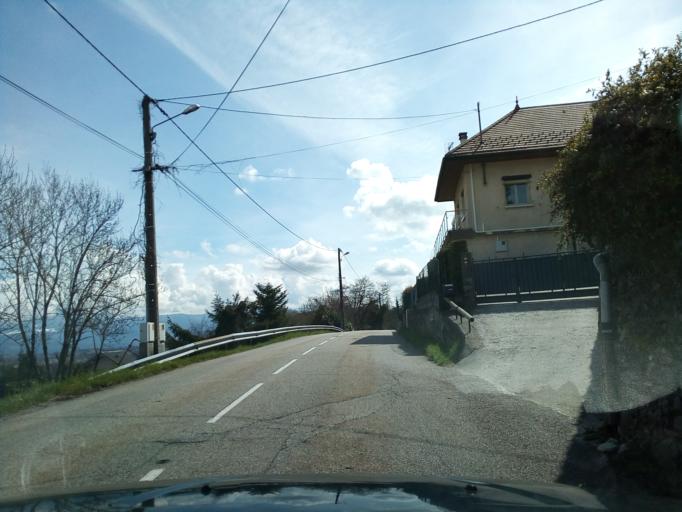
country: FR
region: Rhone-Alpes
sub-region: Departement de la Savoie
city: Barberaz
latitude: 45.5479
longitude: 5.9469
